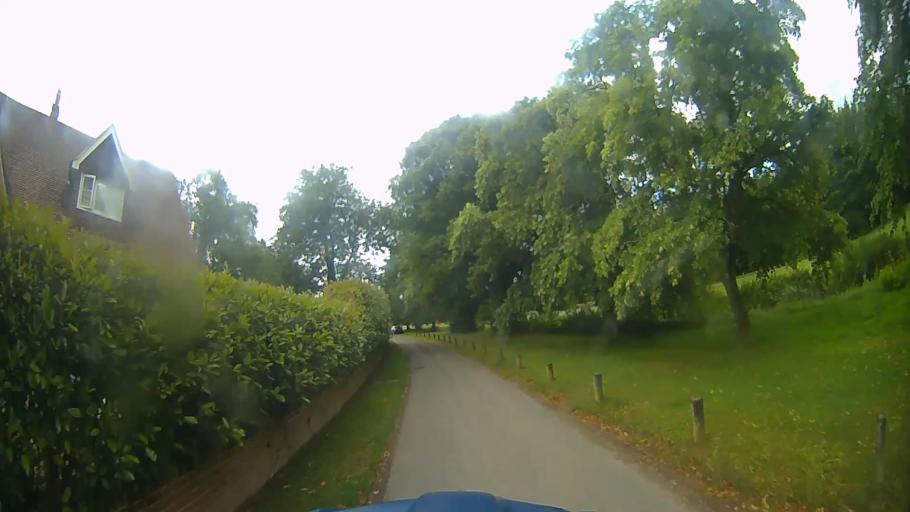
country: GB
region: England
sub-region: Hampshire
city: Four Marks
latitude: 51.1022
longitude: -1.1632
